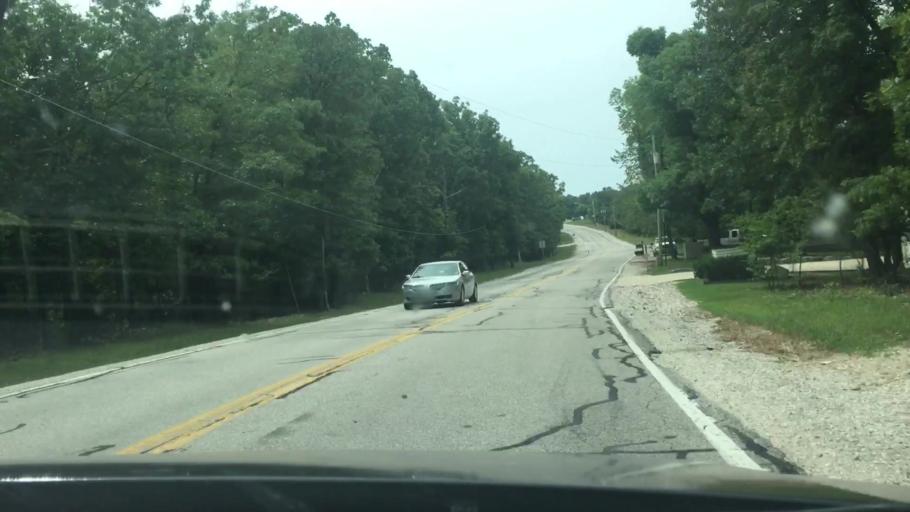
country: US
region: Missouri
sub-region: Camden County
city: Four Seasons
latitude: 38.2050
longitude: -92.7020
